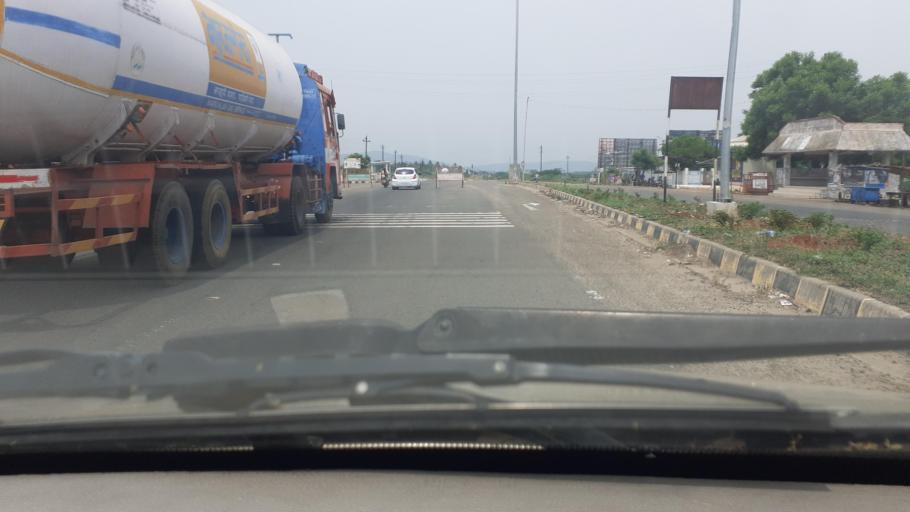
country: IN
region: Tamil Nadu
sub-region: Tirunelveli Kattabo
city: Tirunelveli
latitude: 8.7137
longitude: 77.7900
